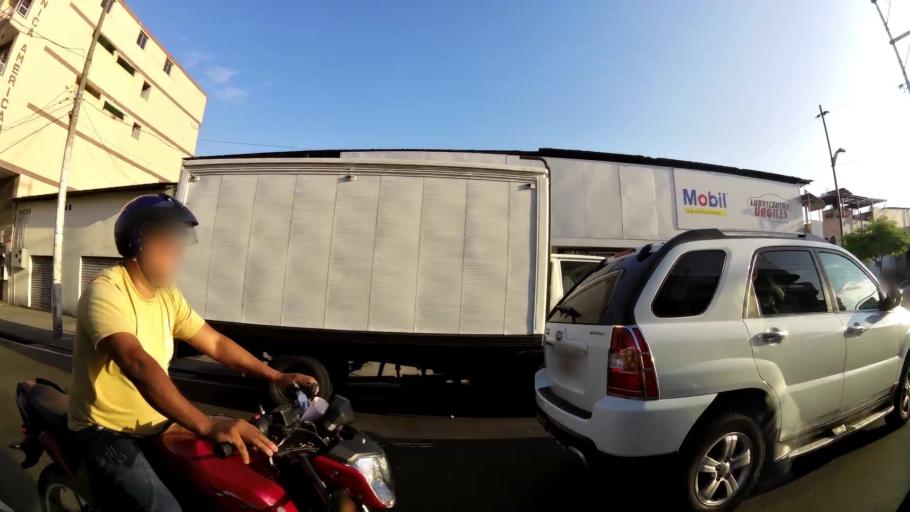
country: EC
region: Guayas
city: Guayaquil
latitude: -2.2083
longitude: -79.8927
